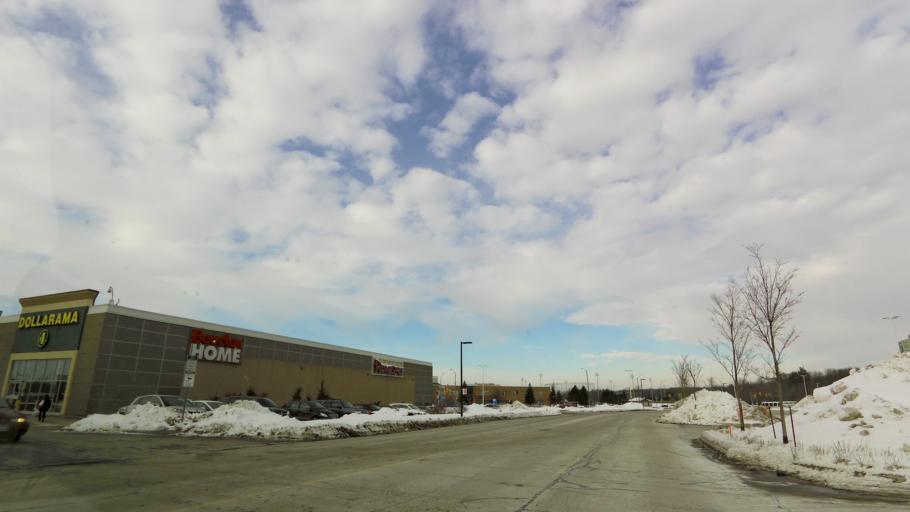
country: CA
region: Ontario
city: Mississauga
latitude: 43.5581
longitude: -79.7148
